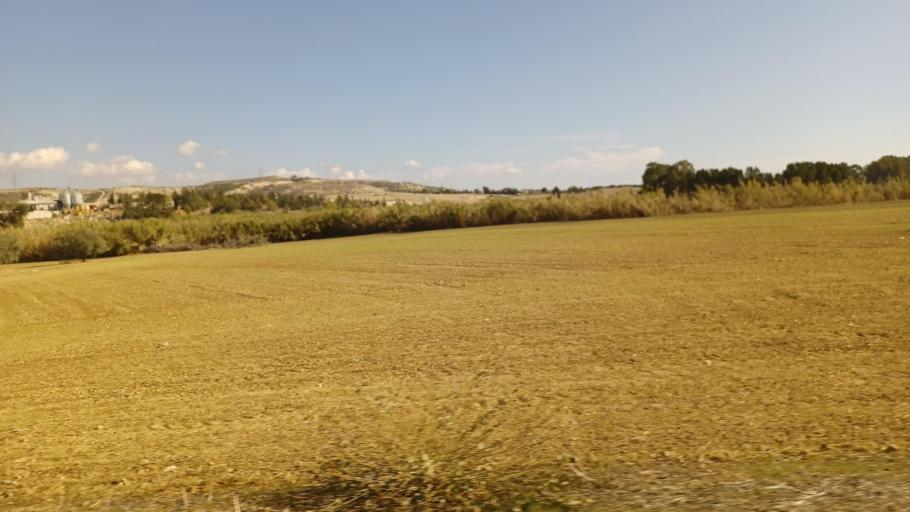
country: CY
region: Larnaka
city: Voroklini
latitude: 34.9992
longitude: 33.6523
